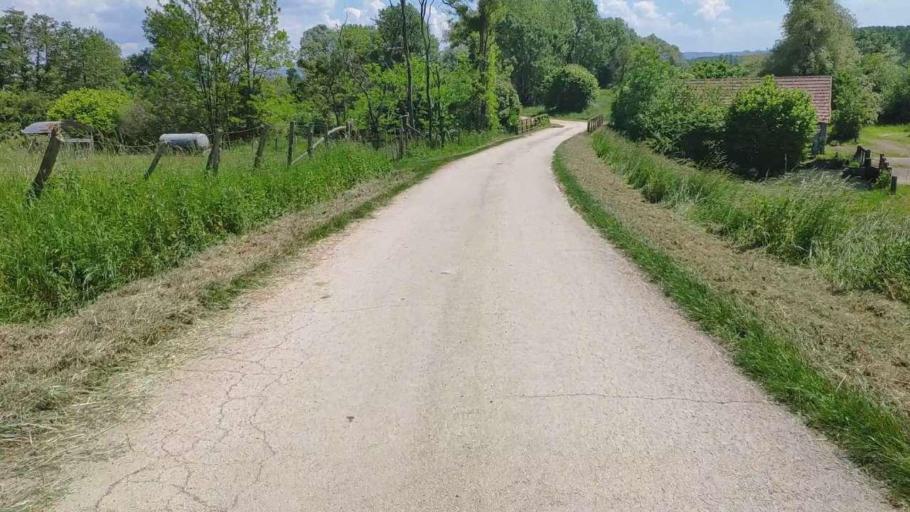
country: FR
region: Franche-Comte
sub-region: Departement du Jura
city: Bletterans
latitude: 46.7399
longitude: 5.3866
